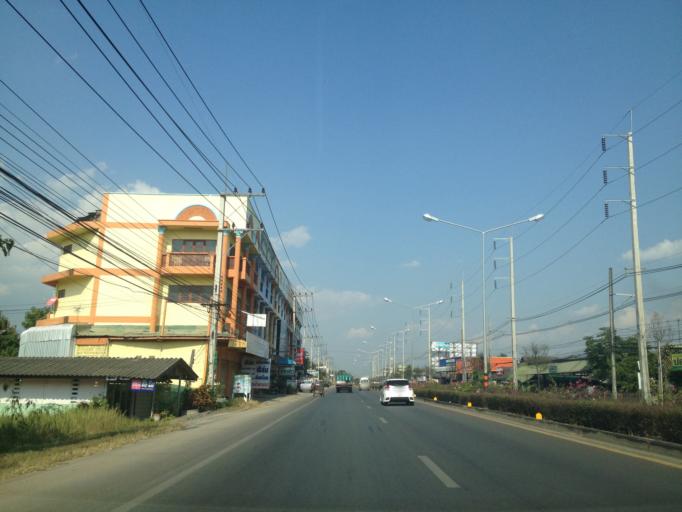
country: TH
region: Chiang Mai
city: San Pa Tong
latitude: 18.6518
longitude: 98.9047
